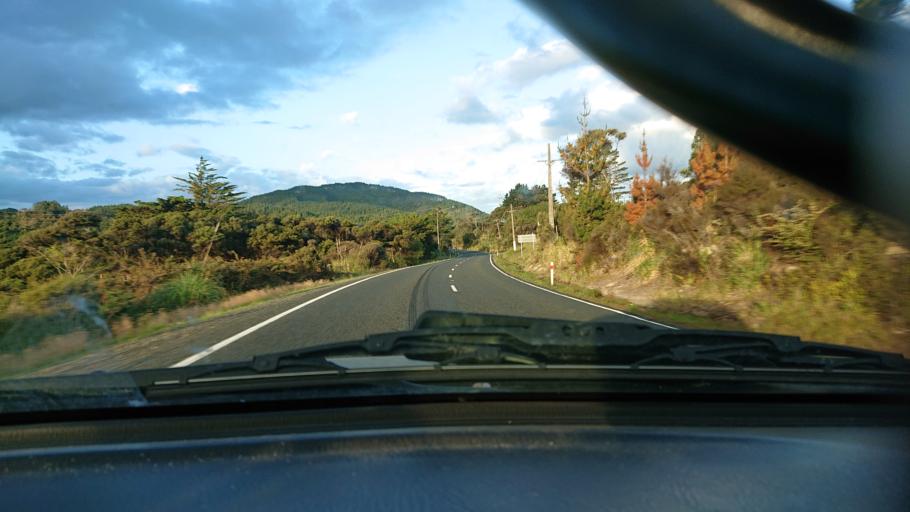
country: NZ
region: Auckland
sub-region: Auckland
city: Parakai
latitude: -36.5104
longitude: 174.4536
